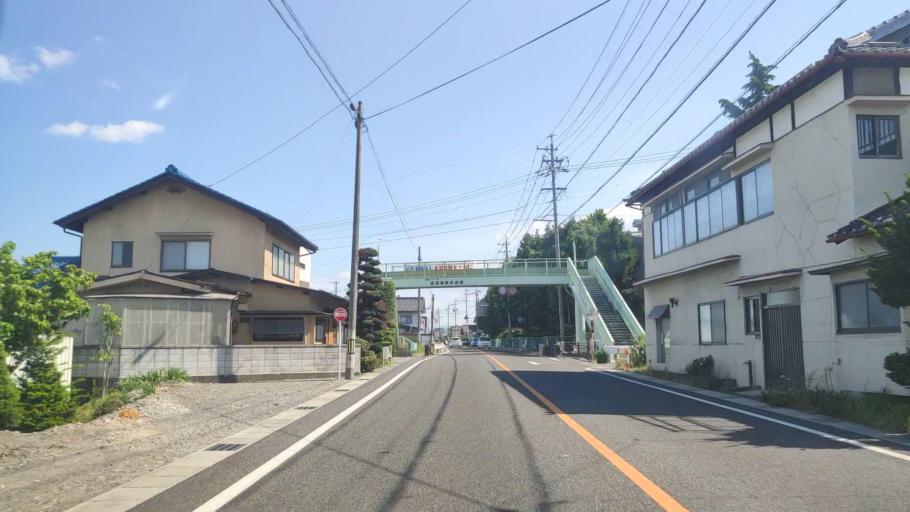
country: JP
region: Nagano
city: Toyoshina
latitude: 36.2952
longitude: 137.9059
